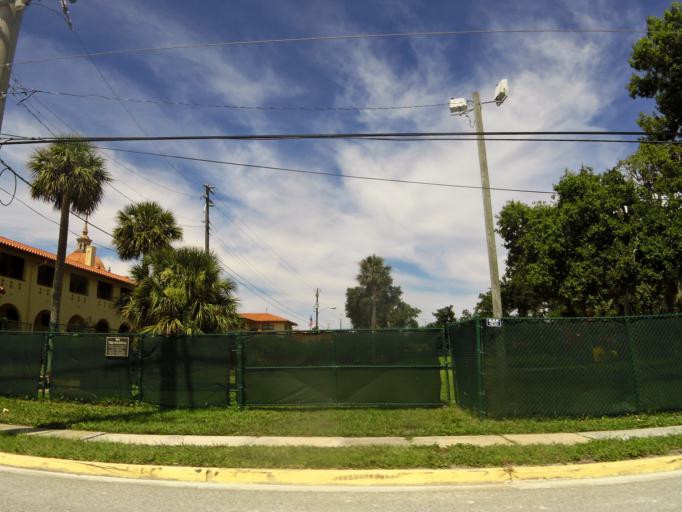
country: US
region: Florida
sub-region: Volusia County
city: Daytona Beach
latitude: 29.2165
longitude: -81.0278
